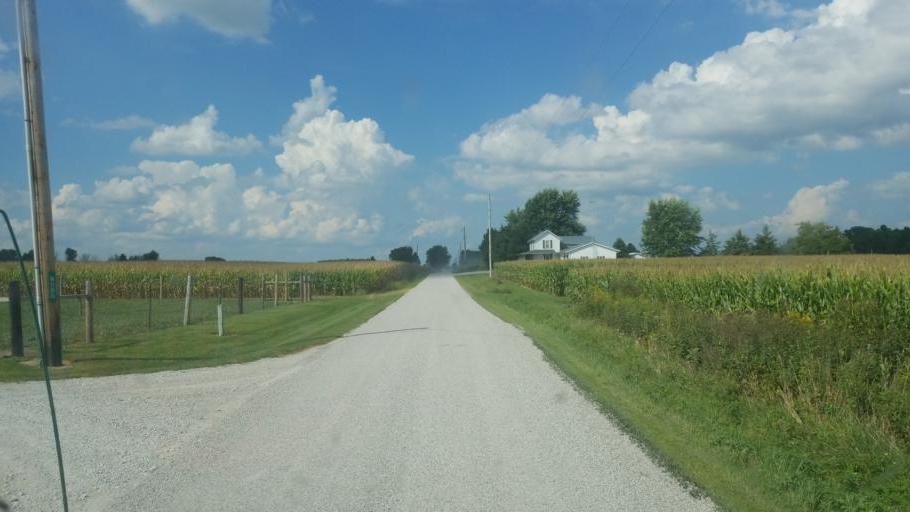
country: US
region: Ohio
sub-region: Huron County
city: Willard
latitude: 40.9888
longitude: -82.7966
